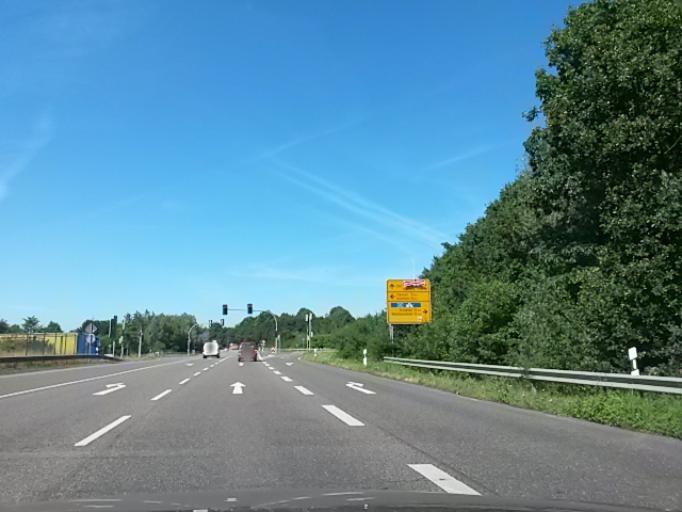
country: DE
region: North Rhine-Westphalia
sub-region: Regierungsbezirk Dusseldorf
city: Grefrath
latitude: 51.3277
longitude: 6.3382
